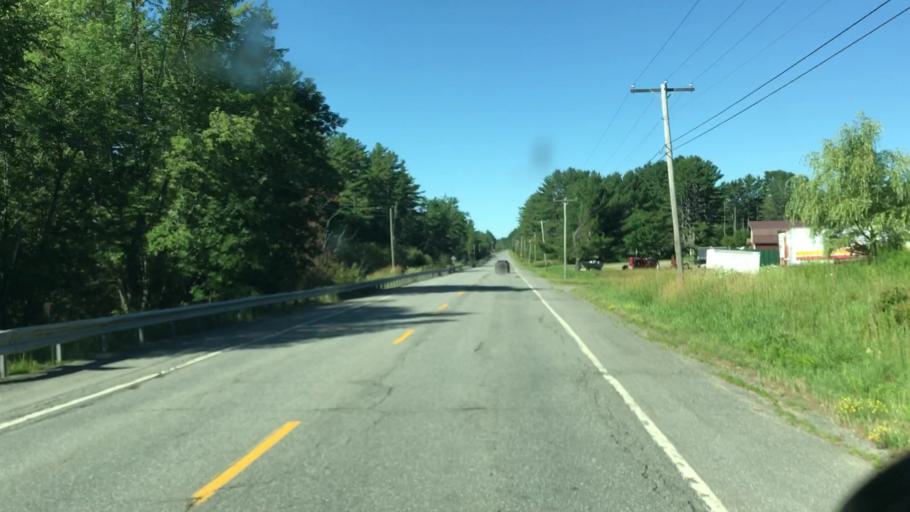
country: US
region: Maine
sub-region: Penobscot County
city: Lincoln
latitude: 45.3334
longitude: -68.5818
